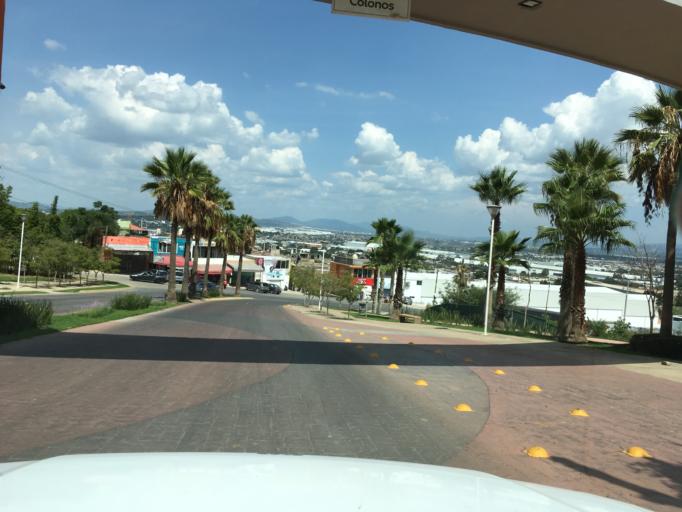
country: MX
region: Jalisco
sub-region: Tlajomulco de Zuniga
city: Altus Bosques
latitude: 20.5877
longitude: -103.3595
